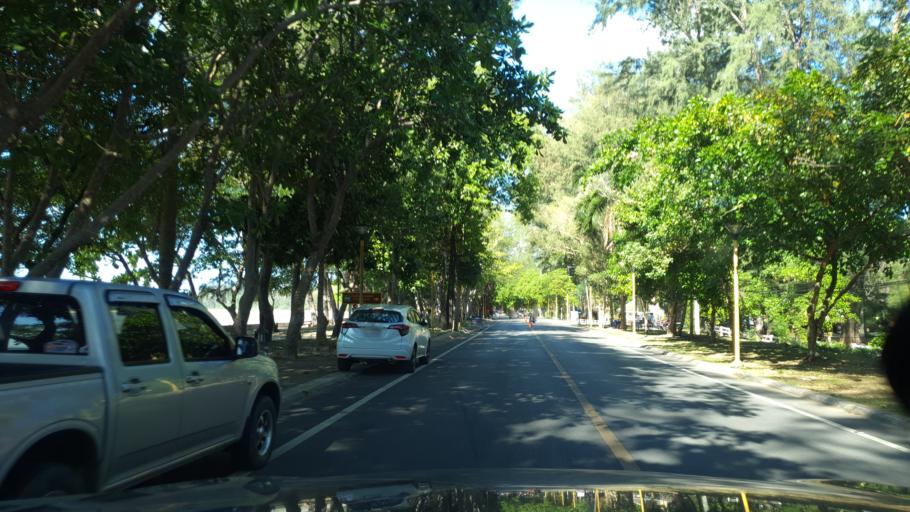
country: TH
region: Phangnga
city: Ban Ao Nang
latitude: 8.0455
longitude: 98.8042
